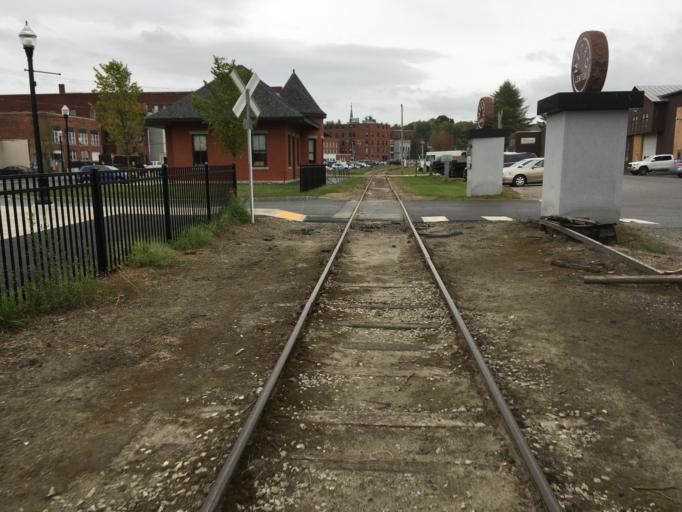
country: US
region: Vermont
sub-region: Washington County
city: Barre
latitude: 44.1989
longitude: -72.5049
